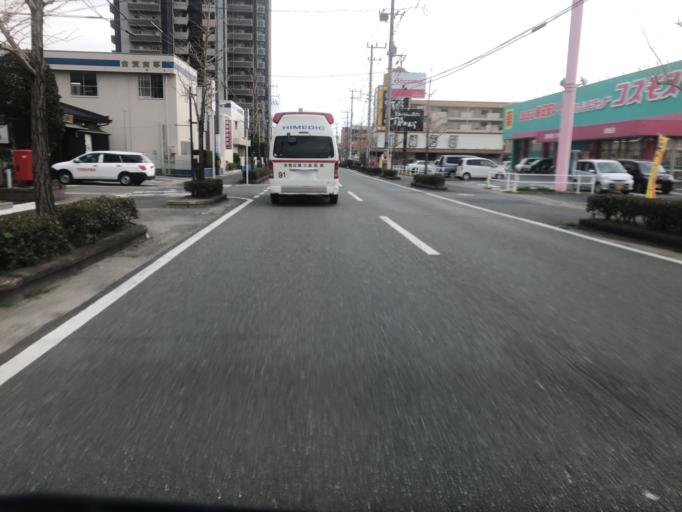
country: JP
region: Saga Prefecture
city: Saga-shi
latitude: 33.2794
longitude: 130.2699
